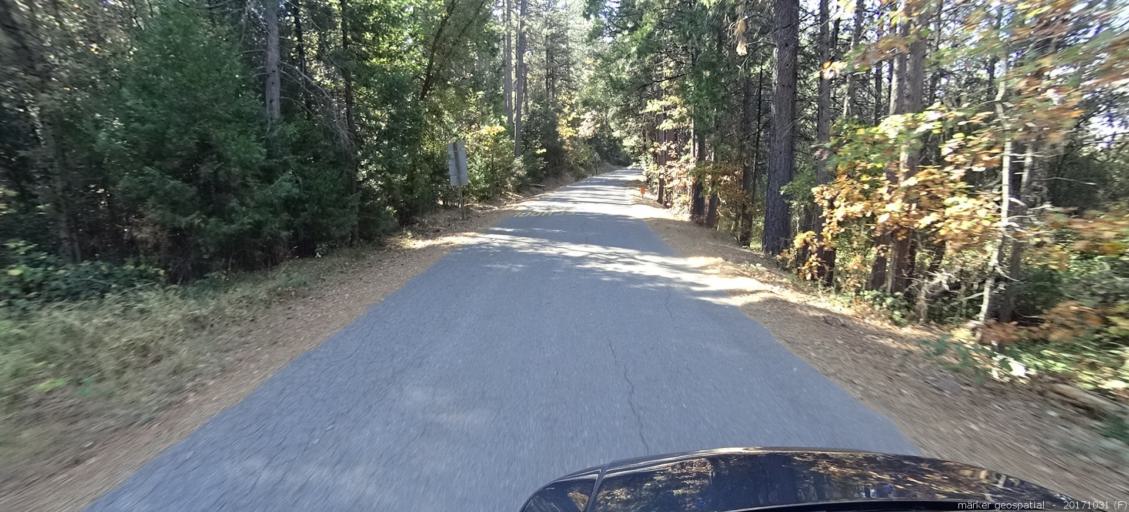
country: US
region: California
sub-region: Shasta County
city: Shingletown
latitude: 40.5119
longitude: -121.9364
